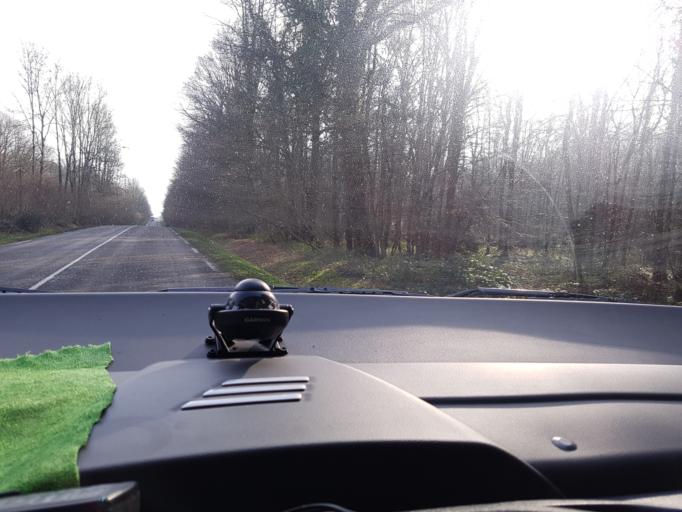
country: FR
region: Picardie
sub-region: Departement de l'Aisne
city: Hirson
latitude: 49.9452
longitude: 4.0681
